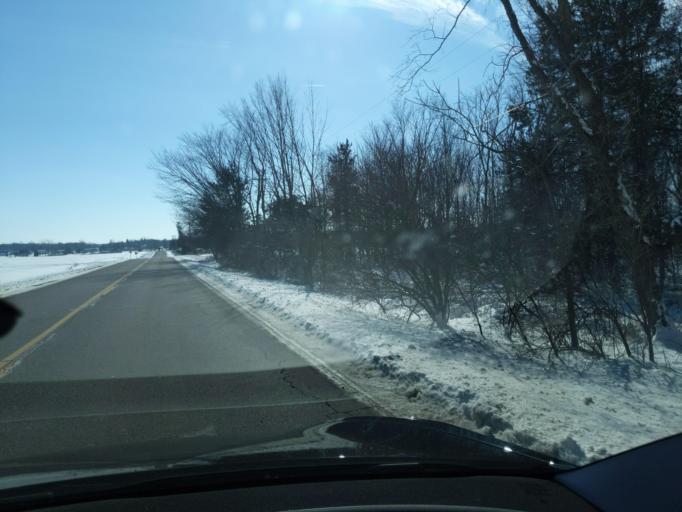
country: US
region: Michigan
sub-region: Livingston County
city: Fowlerville
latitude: 42.6182
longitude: -84.0715
